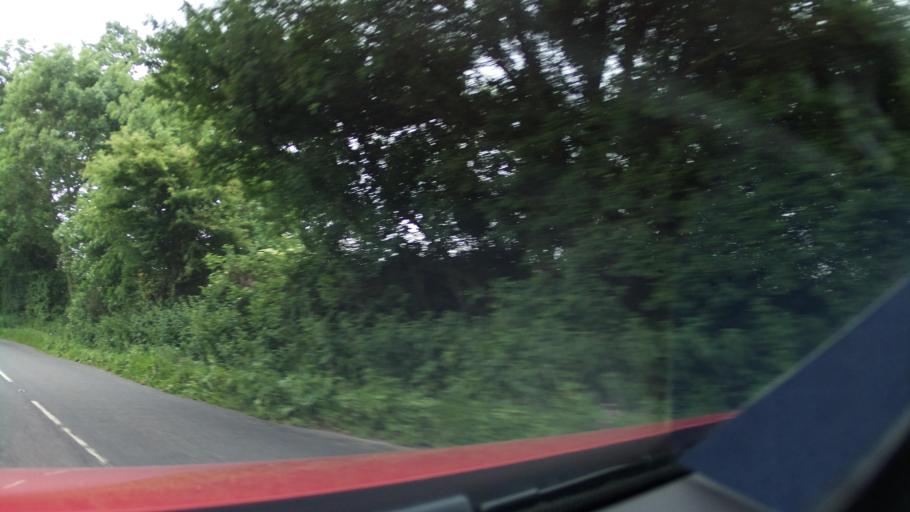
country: GB
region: England
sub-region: Derbyshire
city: Rodsley
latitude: 52.8710
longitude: -1.7227
